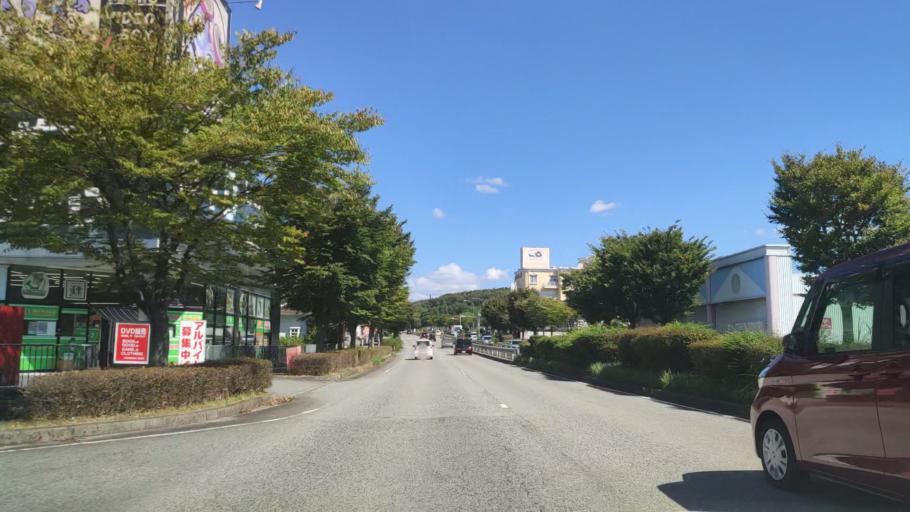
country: JP
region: Hyogo
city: Yashiro
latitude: 34.9399
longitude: 134.9656
